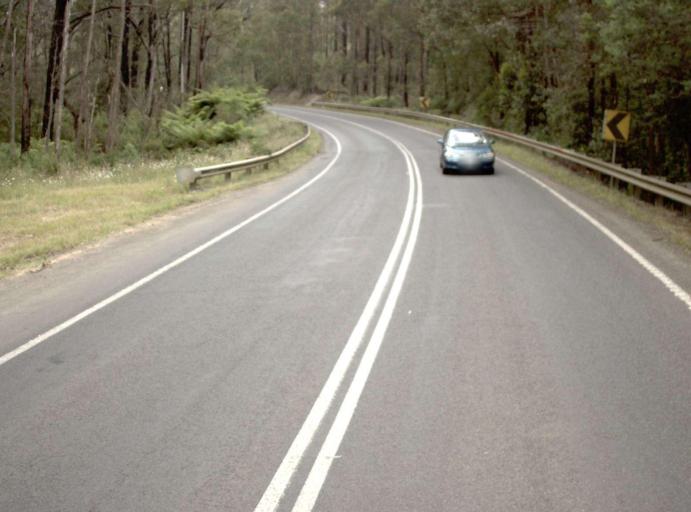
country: AU
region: Victoria
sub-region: Latrobe
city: Moe
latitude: -38.3710
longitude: 146.1803
